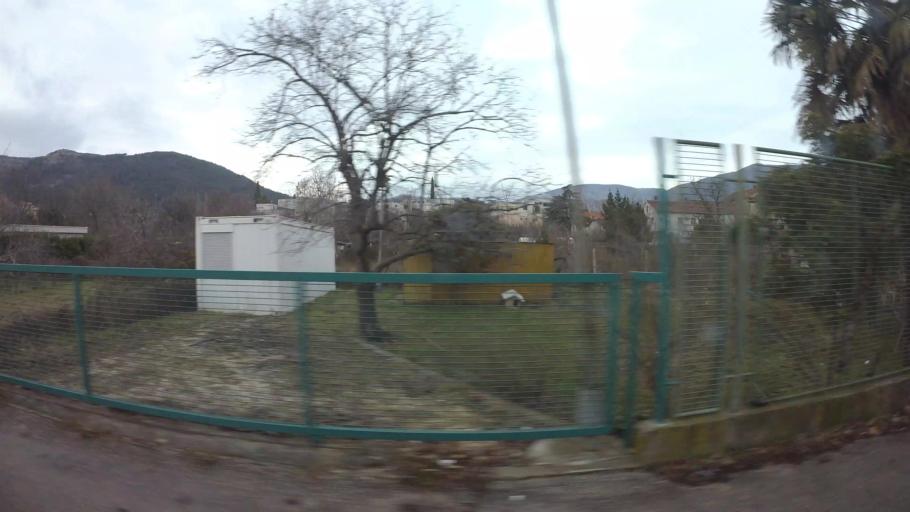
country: BA
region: Federation of Bosnia and Herzegovina
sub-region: Hercegovacko-Bosanski Kanton
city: Mostar
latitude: 43.3403
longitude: 17.8048
